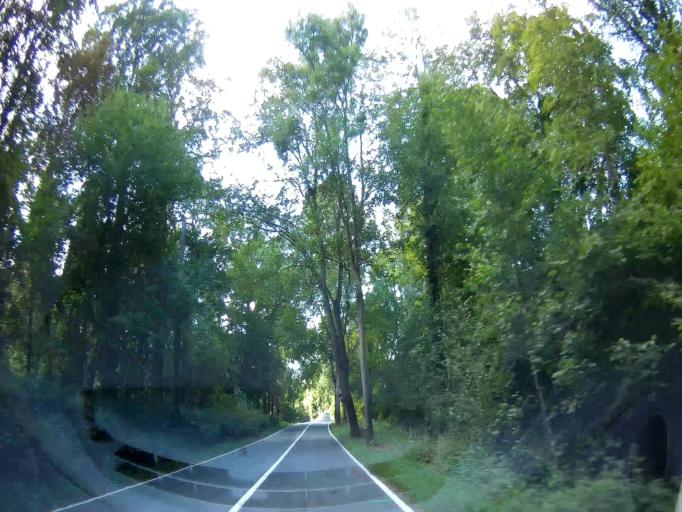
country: BE
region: Wallonia
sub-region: Province de Namur
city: Anhee
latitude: 50.3181
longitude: 4.8578
